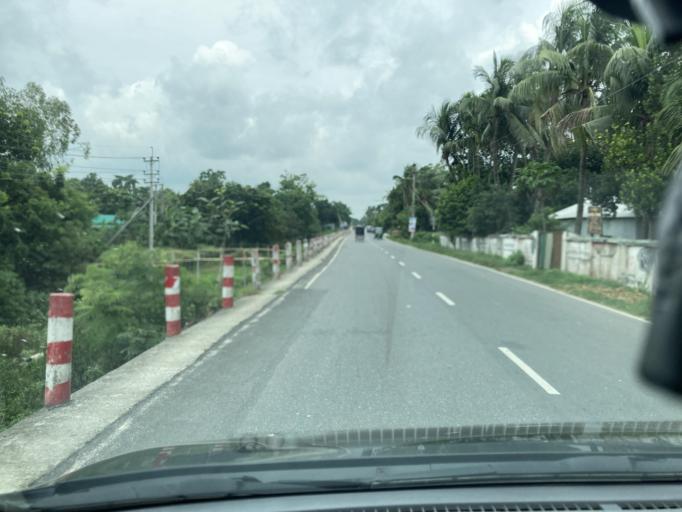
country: BD
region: Dhaka
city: Azimpur
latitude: 23.8057
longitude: 90.2134
